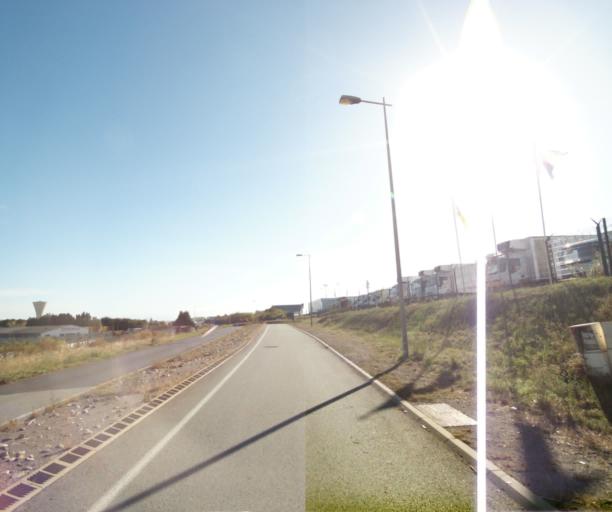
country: FR
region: Auvergne
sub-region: Departement du Puy-de-Dome
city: Gerzat
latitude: 45.8368
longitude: 3.1354
